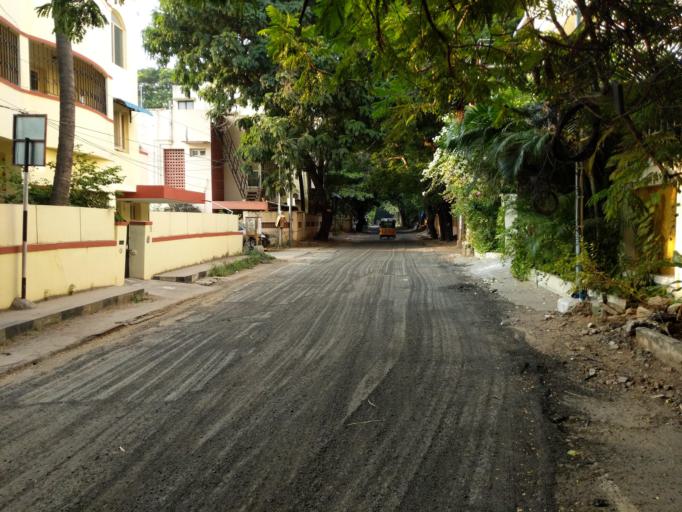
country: IN
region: Tamil Nadu
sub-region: Chennai
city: Gandhi Nagar
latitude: 13.0052
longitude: 80.2607
